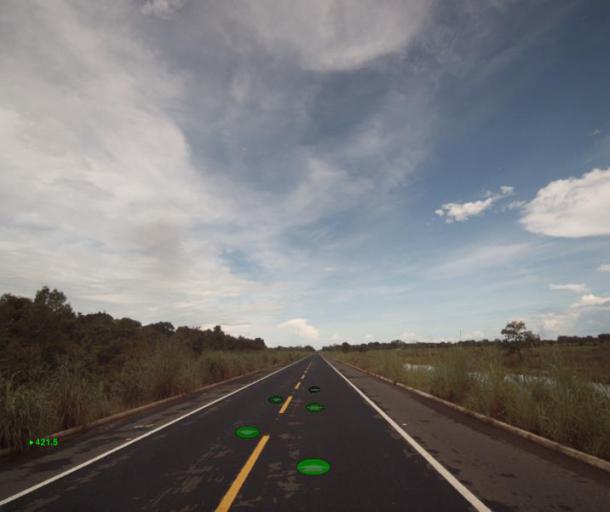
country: BR
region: Goias
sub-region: Sao Miguel Do Araguaia
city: Sao Miguel do Araguaia
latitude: -13.2435
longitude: -50.5373
